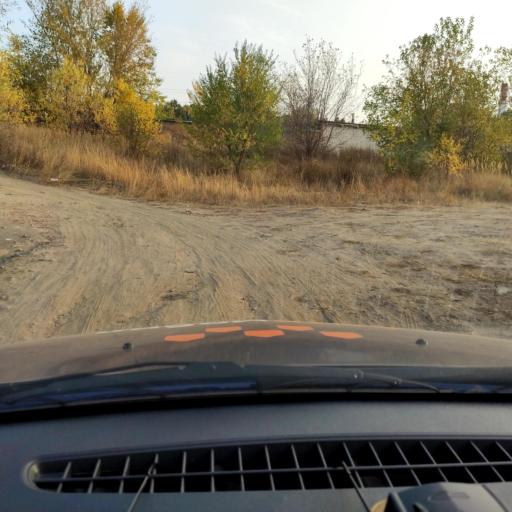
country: RU
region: Voronezj
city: Pridonskoy
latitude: 51.6643
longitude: 39.1128
